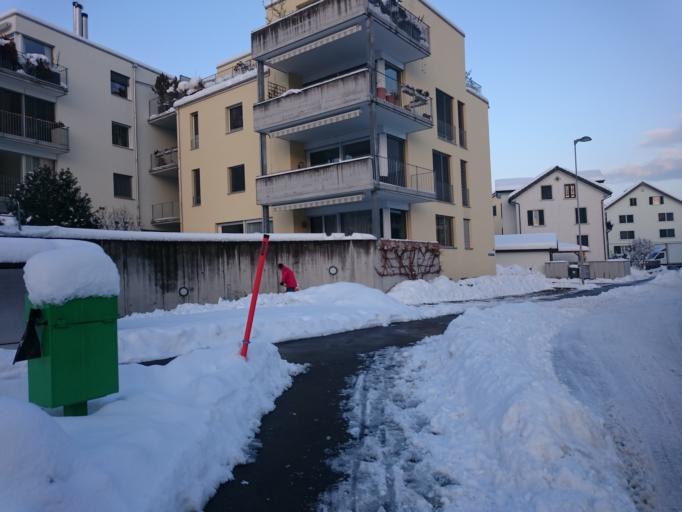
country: CH
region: Zurich
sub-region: Bezirk Hinwil
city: Rueti / Westlicher Dorfteil
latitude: 47.2583
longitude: 8.8460
